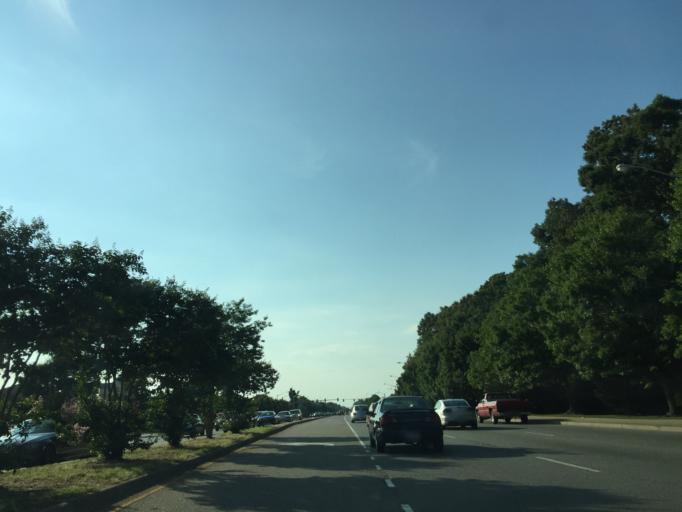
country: US
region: Virginia
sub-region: York County
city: Yorktown
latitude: 37.1288
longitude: -76.5123
